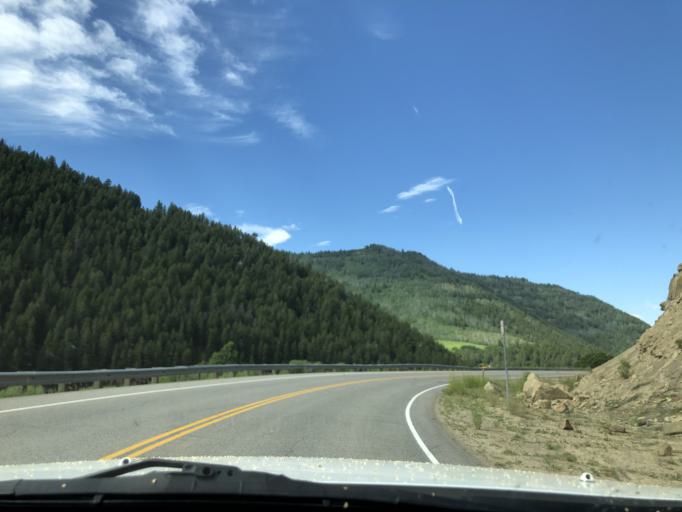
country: US
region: Colorado
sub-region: Delta County
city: Paonia
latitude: 38.9437
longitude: -107.3502
